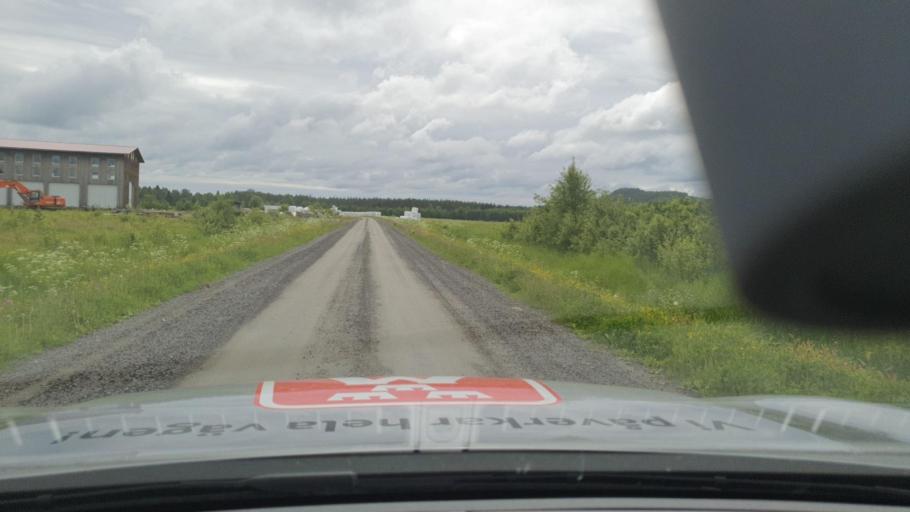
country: SE
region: Norrbotten
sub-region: Lulea Kommun
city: Ranea
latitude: 65.9474
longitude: 22.0955
